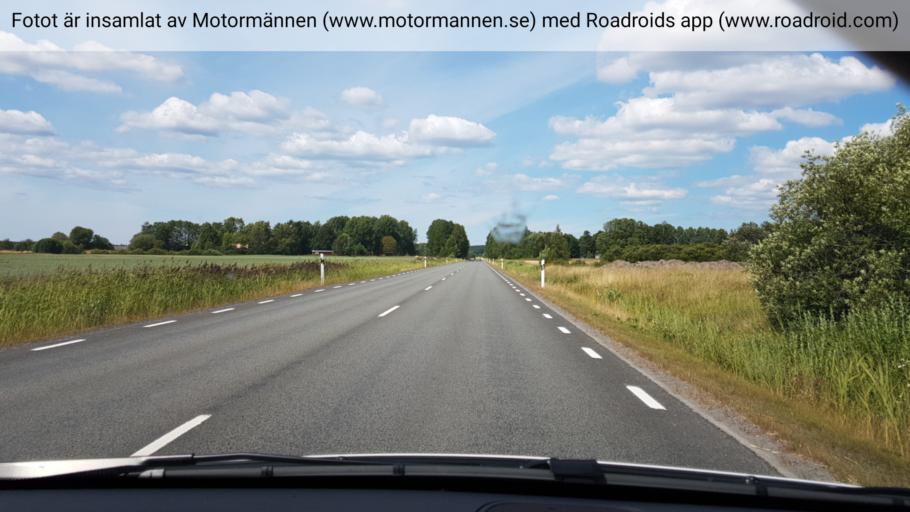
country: SE
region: Vaestra Goetaland
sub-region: Mariestads Kommun
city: Mariestad
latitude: 58.6502
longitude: 13.9013
